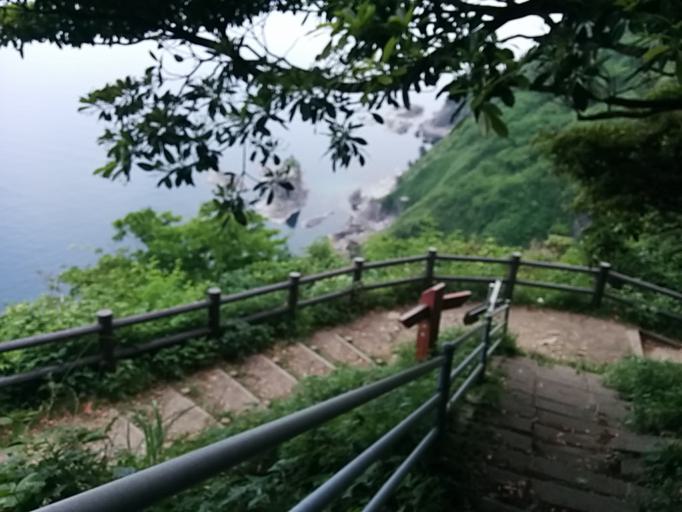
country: JP
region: Kyoto
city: Miyazu
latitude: 35.7749
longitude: 135.2240
